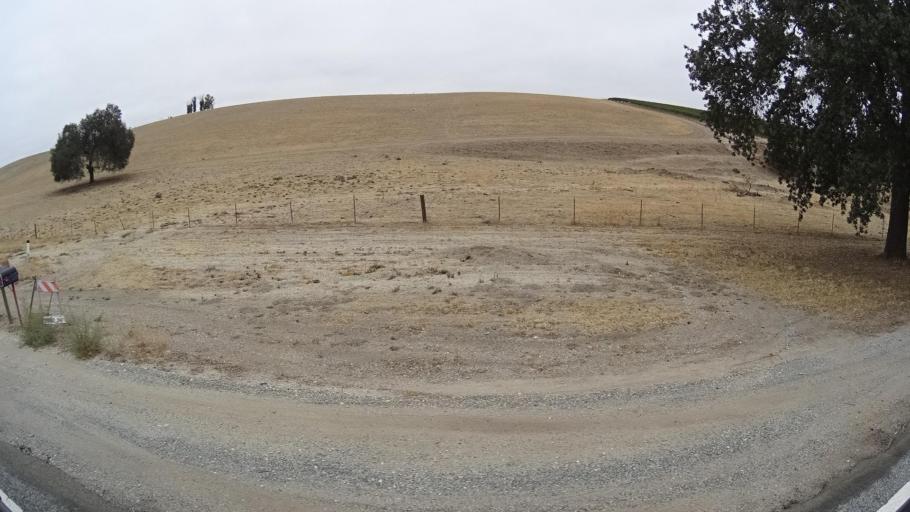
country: US
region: California
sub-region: San Luis Obispo County
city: Lake Nacimiento
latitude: 35.8937
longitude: -120.9336
